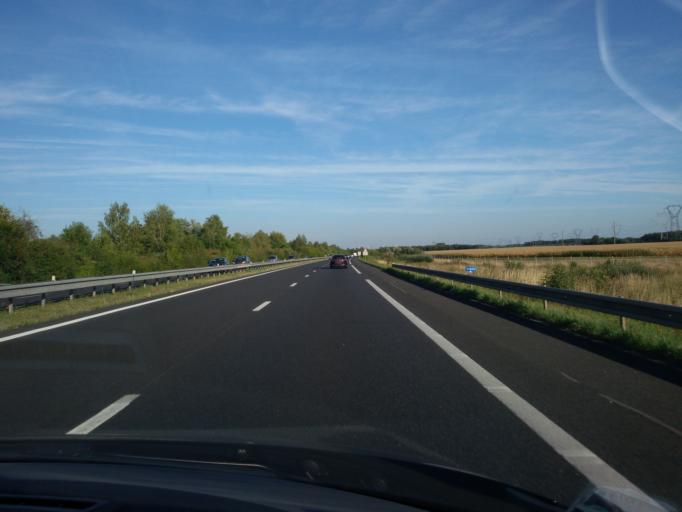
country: FR
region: Centre
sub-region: Departement du Cher
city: Marmagne
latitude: 47.0718
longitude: 2.2809
